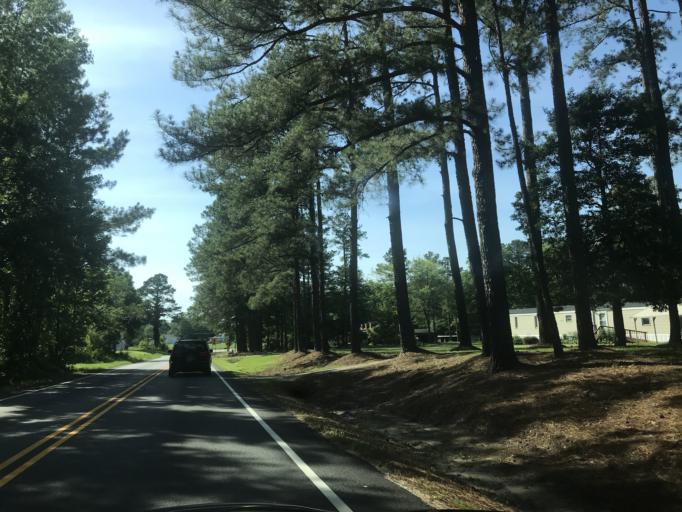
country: US
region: North Carolina
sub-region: Wake County
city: Garner
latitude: 35.6682
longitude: -78.5731
